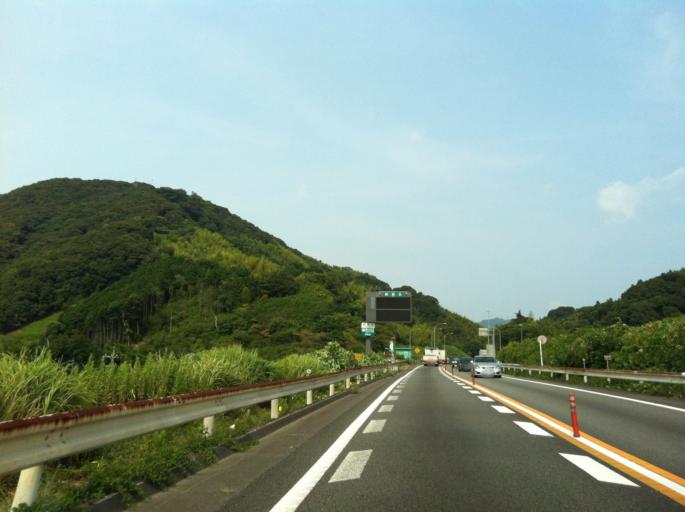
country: JP
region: Shizuoka
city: Fujieda
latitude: 34.8922
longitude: 138.2631
